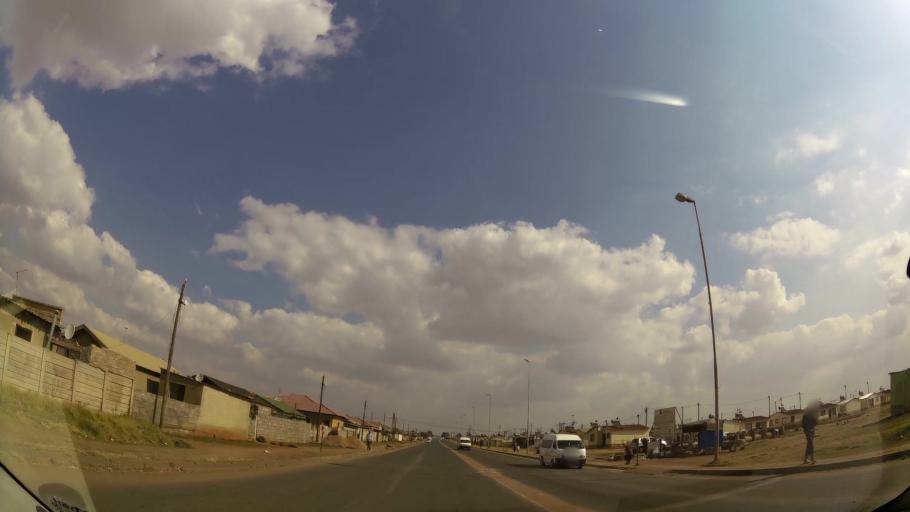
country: ZA
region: Gauteng
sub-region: Ekurhuleni Metropolitan Municipality
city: Springs
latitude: -26.1235
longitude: 28.4524
